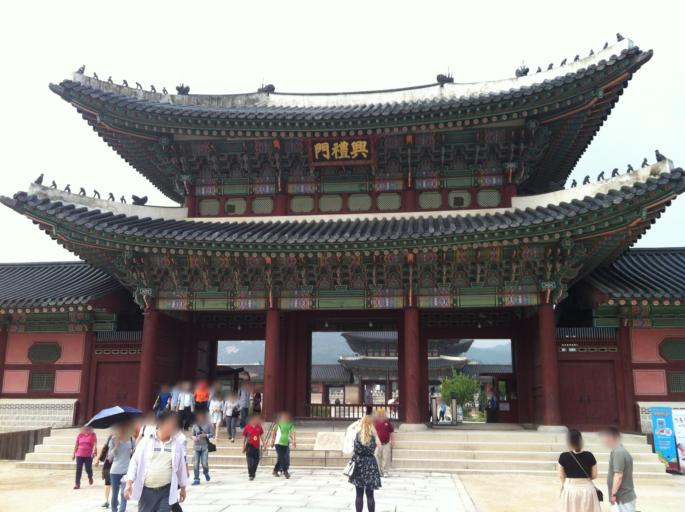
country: KR
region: Seoul
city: Seoul
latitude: 37.5767
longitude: 126.9768
